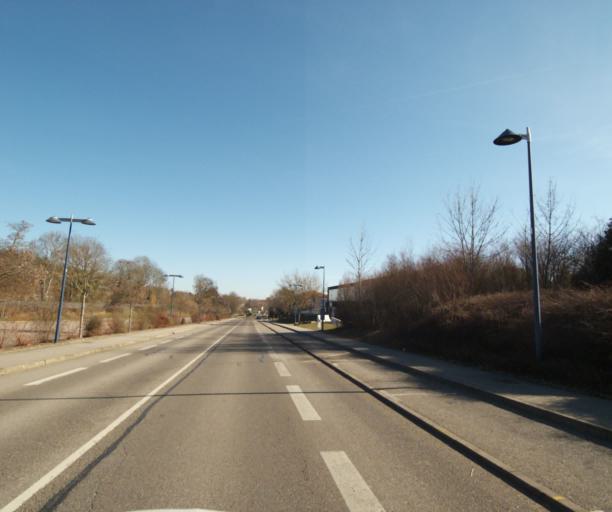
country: FR
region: Lorraine
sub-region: Departement de Meurthe-et-Moselle
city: Ludres
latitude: 48.6192
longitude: 6.1652
